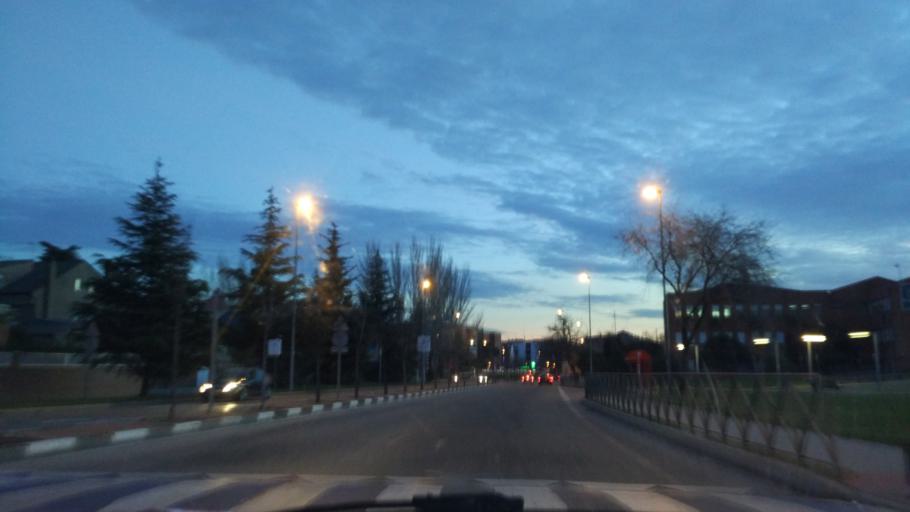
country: ES
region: Madrid
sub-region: Provincia de Madrid
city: Leganes
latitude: 40.3380
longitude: -3.7702
